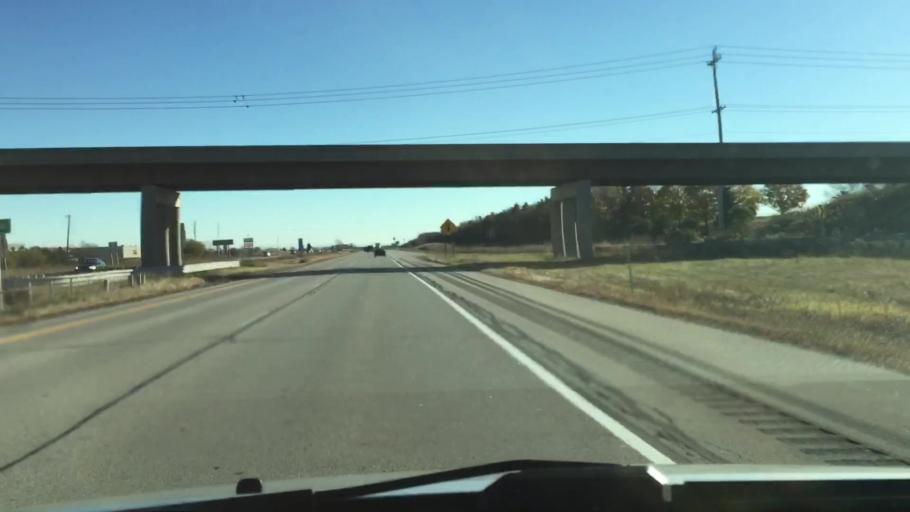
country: US
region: Wisconsin
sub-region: Outagamie County
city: Kimberly
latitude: 44.2979
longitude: -88.3540
